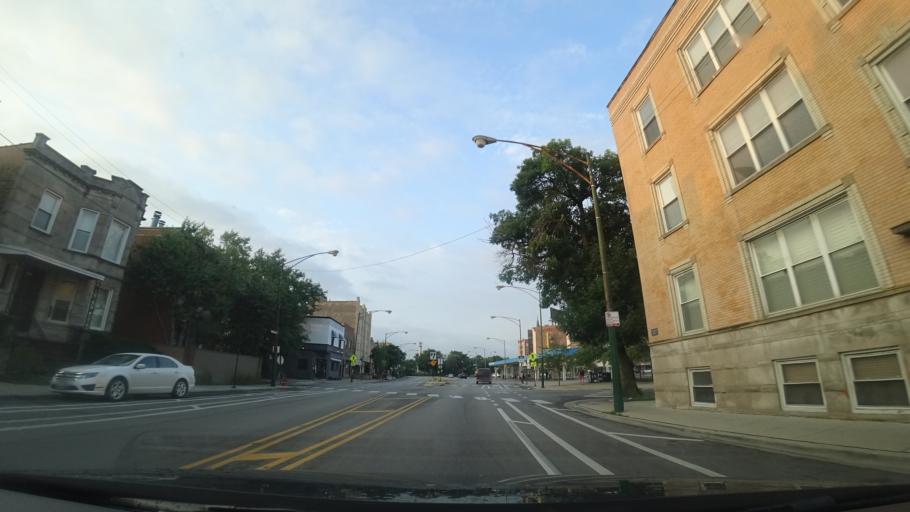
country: US
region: Illinois
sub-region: Cook County
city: Lincolnwood
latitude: 41.9305
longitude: -87.7074
